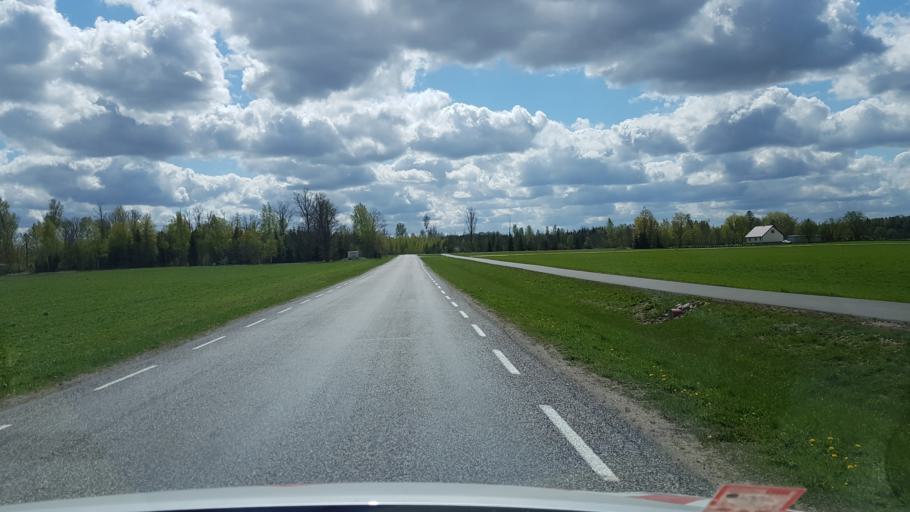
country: EE
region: Jogevamaa
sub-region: Poltsamaa linn
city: Poltsamaa
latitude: 58.6989
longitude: 25.9419
